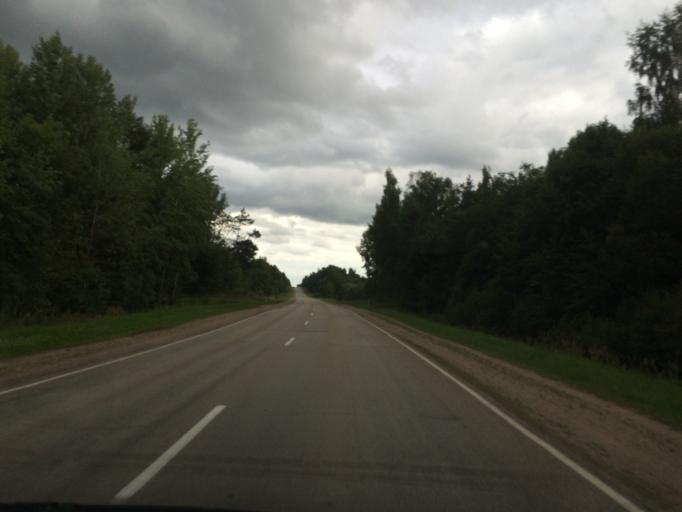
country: LV
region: Rezekne
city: Rezekne
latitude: 56.5684
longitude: 27.3689
